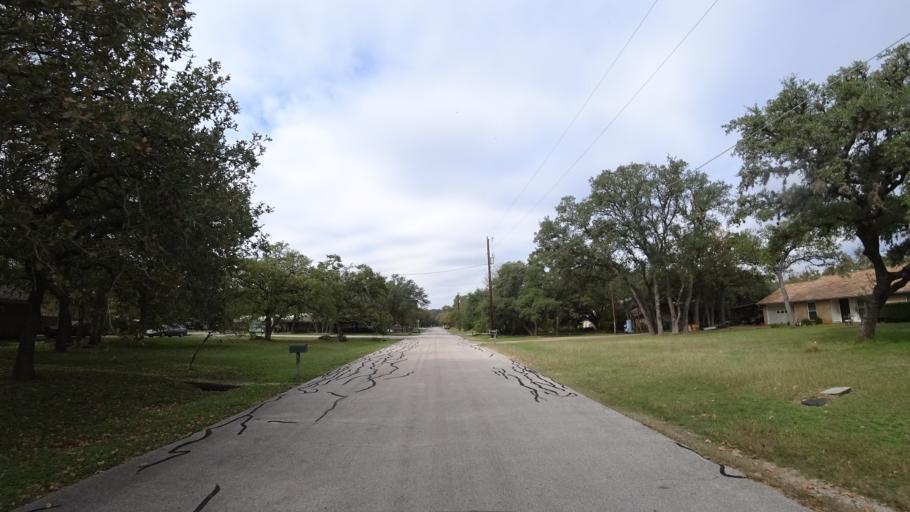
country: US
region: Texas
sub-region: Travis County
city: Shady Hollow
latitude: 30.1389
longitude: -97.8895
